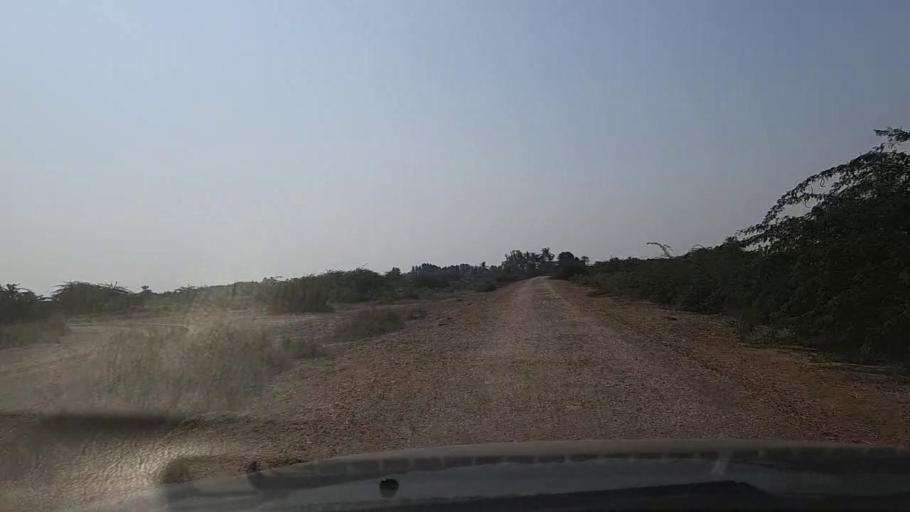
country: PK
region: Sindh
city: Mirpur Sakro
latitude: 24.4041
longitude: 67.6723
